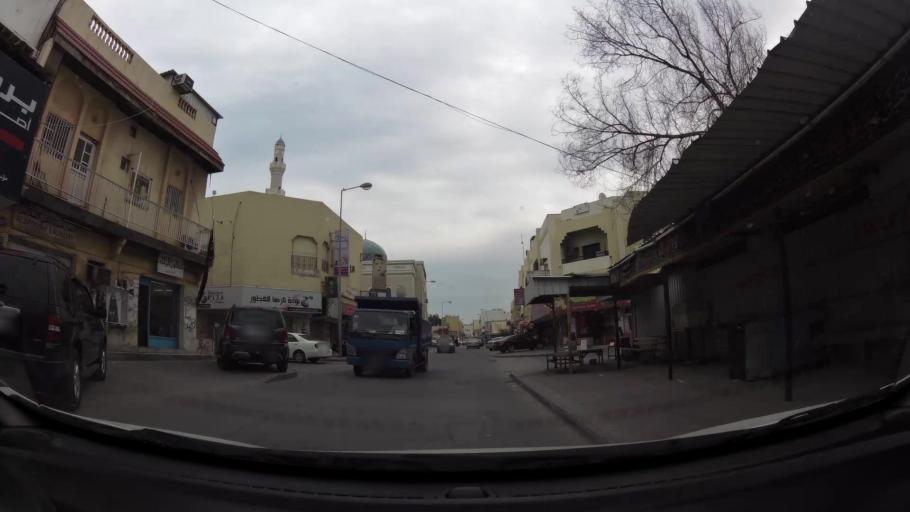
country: BH
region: Northern
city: Sitrah
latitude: 26.1631
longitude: 50.6147
